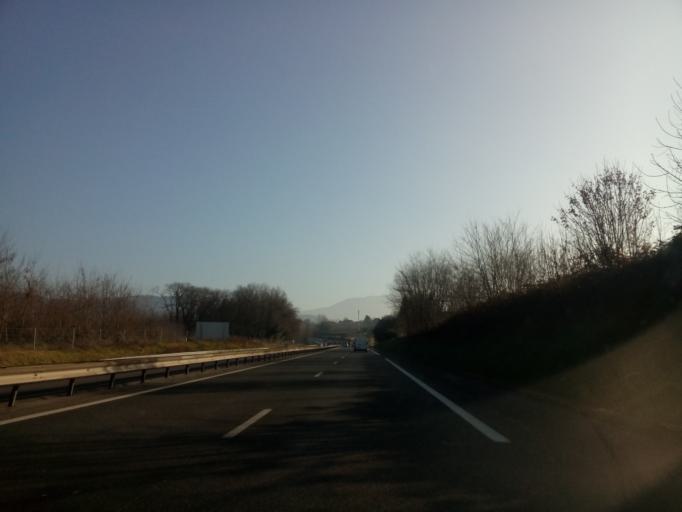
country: FR
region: Rhone-Alpes
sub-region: Departement de la Savoie
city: Le Pont-de-Beauvoisin
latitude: 45.5627
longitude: 5.6829
